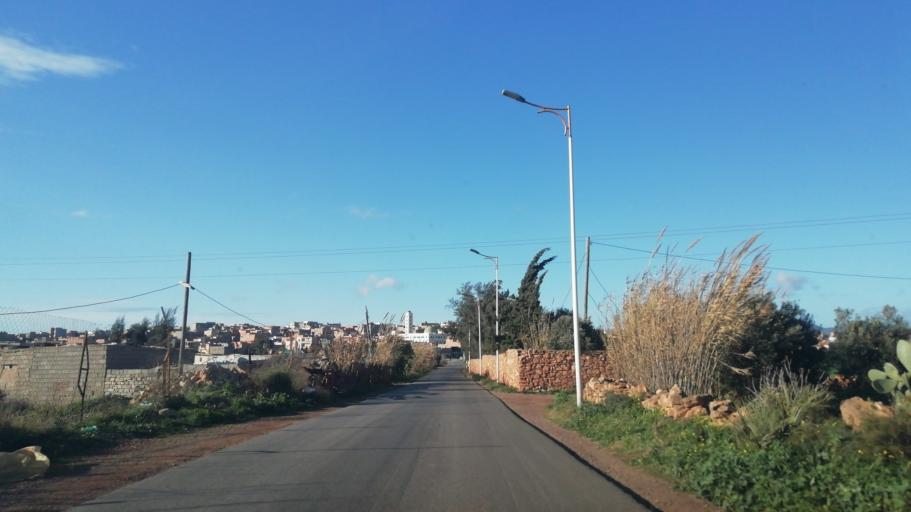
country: DZ
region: Oran
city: Sidi ech Chahmi
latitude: 35.6855
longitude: -0.4945
